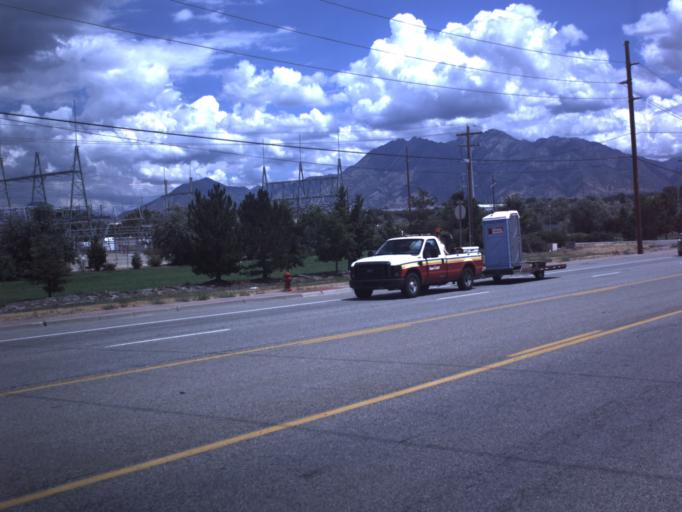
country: US
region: Utah
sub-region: Salt Lake County
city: South Jordan
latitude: 40.5877
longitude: -111.9166
